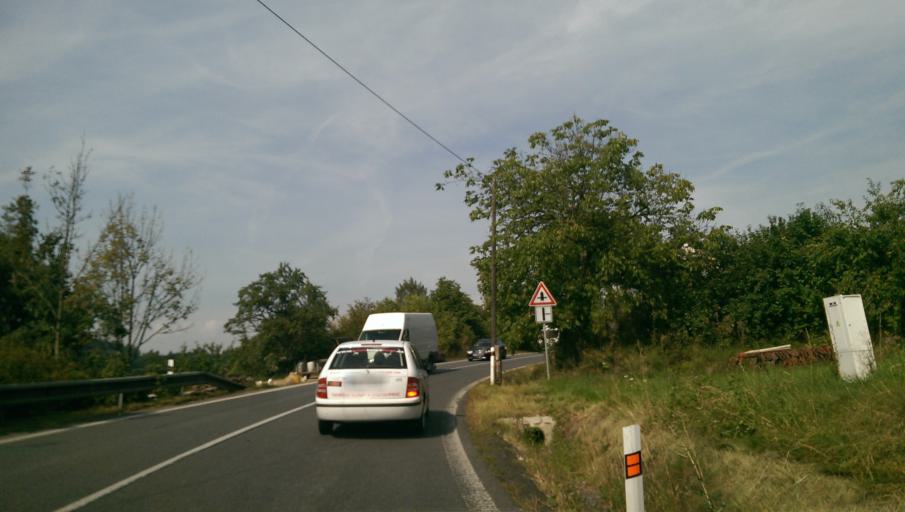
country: CZ
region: Liberecky
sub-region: Okres Semily
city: Turnov
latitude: 50.6070
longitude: 15.1645
